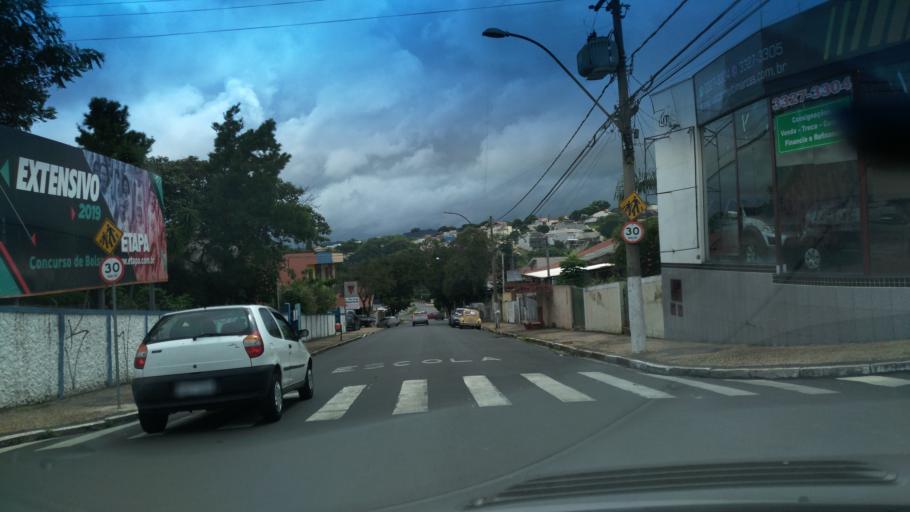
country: BR
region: Sao Paulo
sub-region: Valinhos
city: Valinhos
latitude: -22.9643
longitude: -46.9896
